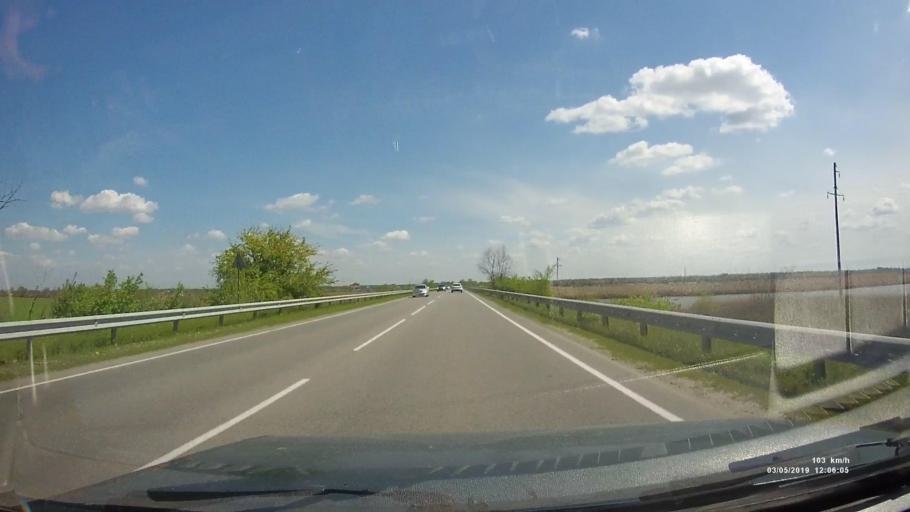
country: RU
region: Rostov
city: Bagayevskaya
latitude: 47.2860
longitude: 40.4426
